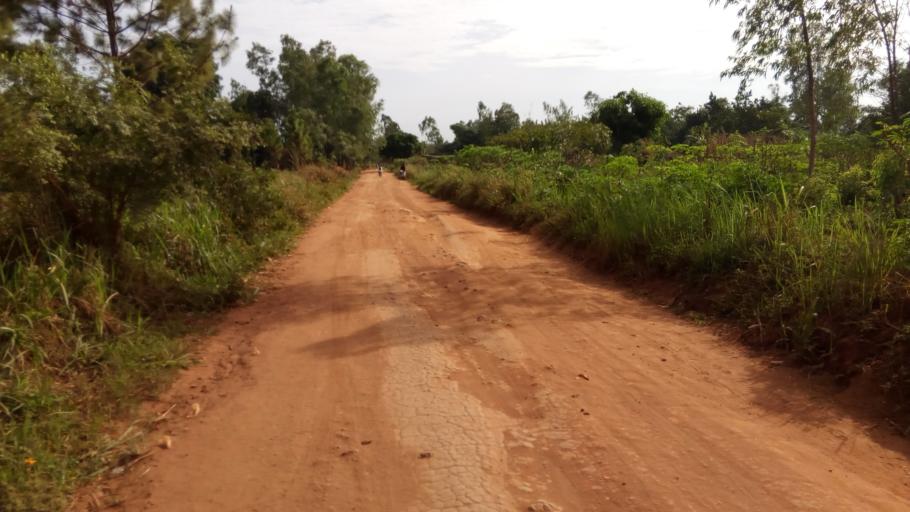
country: UG
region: Northern Region
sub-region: Gulu District
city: Gulu
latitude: 2.7901
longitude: 32.3229
